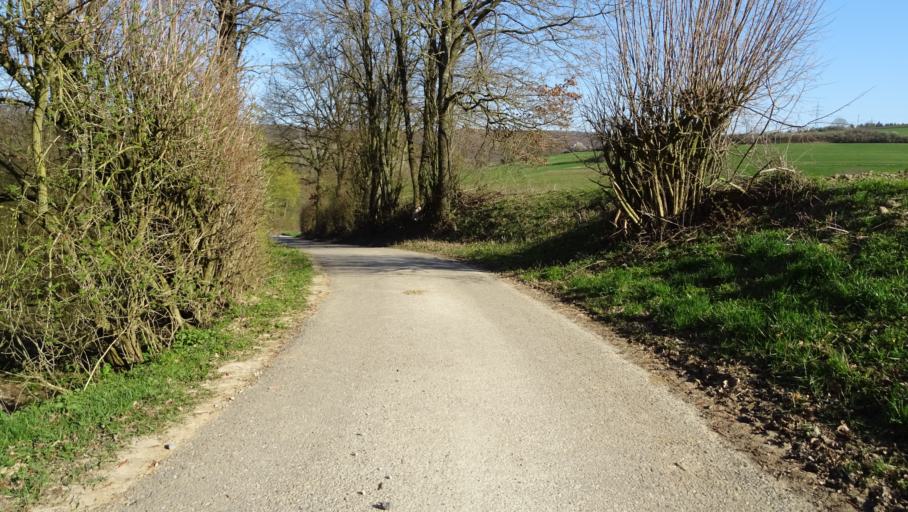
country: DE
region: Baden-Wuerttemberg
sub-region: Karlsruhe Region
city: Binau
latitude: 49.3452
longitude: 9.0492
